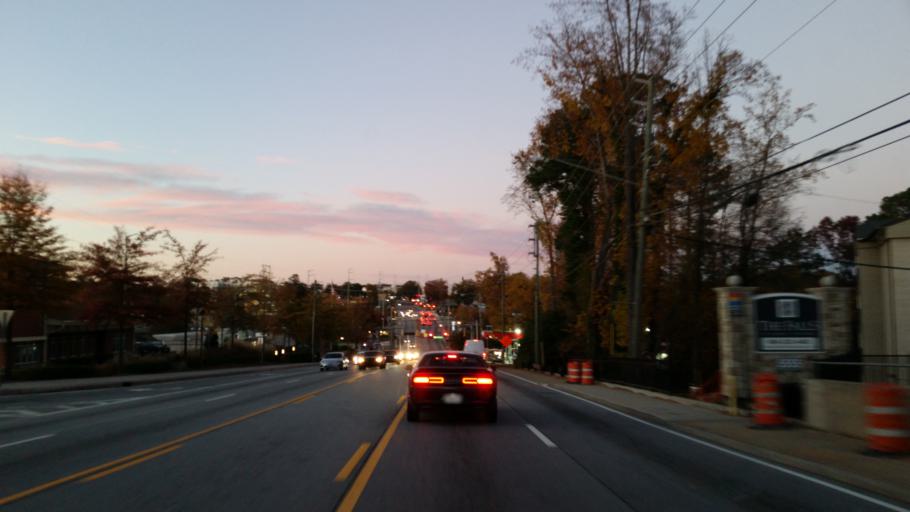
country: US
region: Georgia
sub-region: Fulton County
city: Sandy Springs
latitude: 33.9075
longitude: -84.3787
